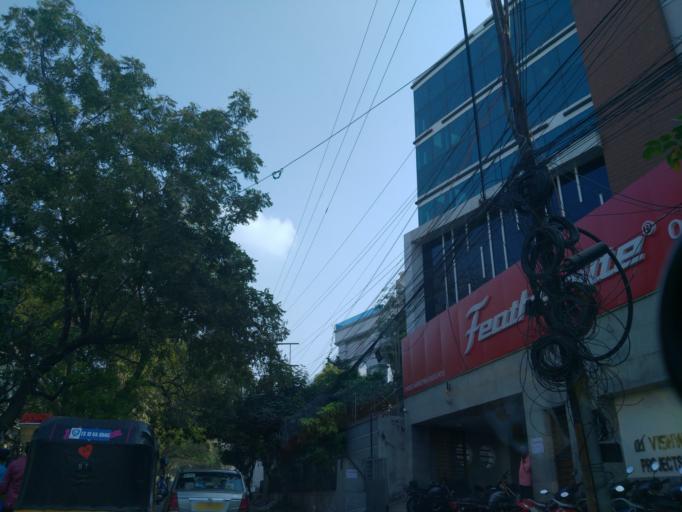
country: IN
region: Telangana
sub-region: Rangareddi
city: Kukatpalli
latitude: 17.4331
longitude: 78.4015
